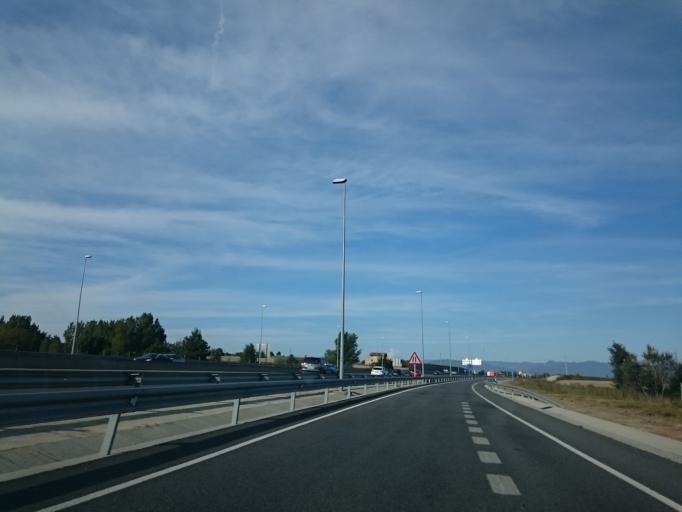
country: ES
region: Catalonia
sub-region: Provincia de Barcelona
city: Gurb
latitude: 41.9461
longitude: 2.2316
